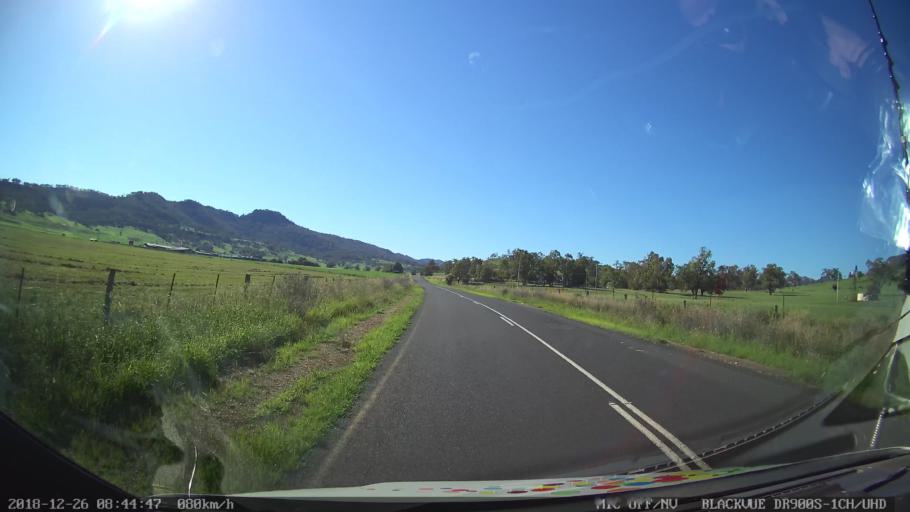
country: AU
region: New South Wales
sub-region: Mid-Western Regional
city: Kandos
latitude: -32.5186
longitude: 150.0815
